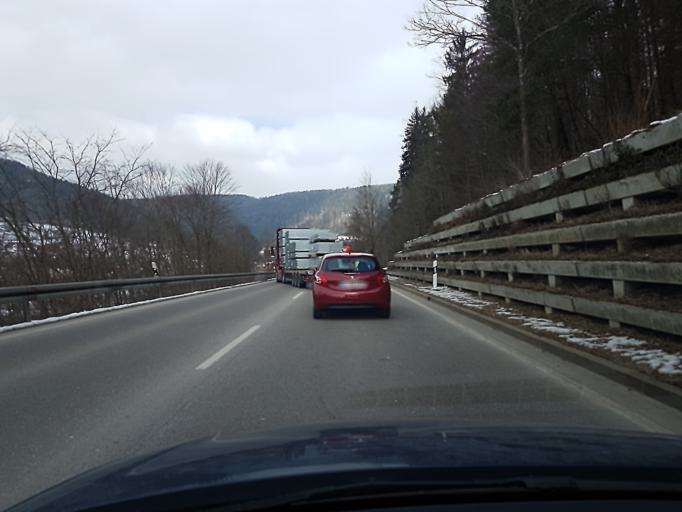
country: DE
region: Baden-Wuerttemberg
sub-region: Freiburg Region
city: Sulz am Neckar
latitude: 48.4155
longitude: 8.6379
